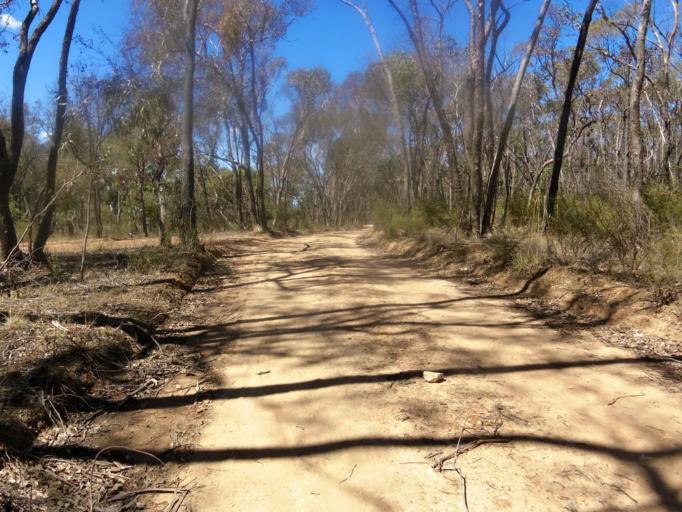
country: AU
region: Victoria
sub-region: Mount Alexander
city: Castlemaine
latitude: -36.9982
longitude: 144.1065
